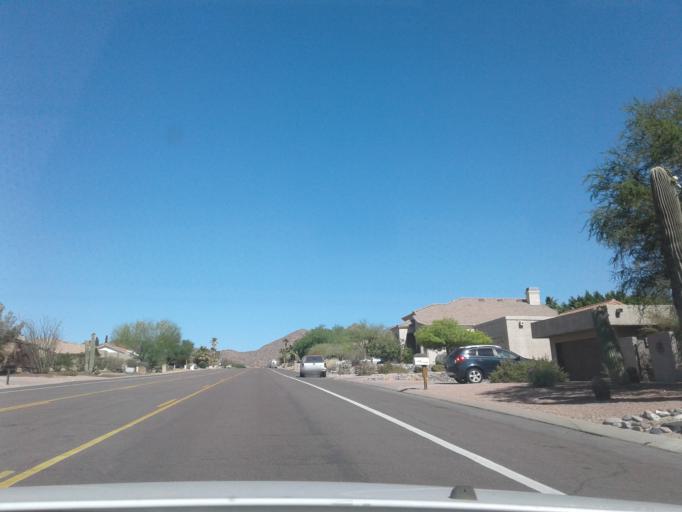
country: US
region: Arizona
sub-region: Maricopa County
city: Fountain Hills
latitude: 33.5944
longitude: -111.7529
